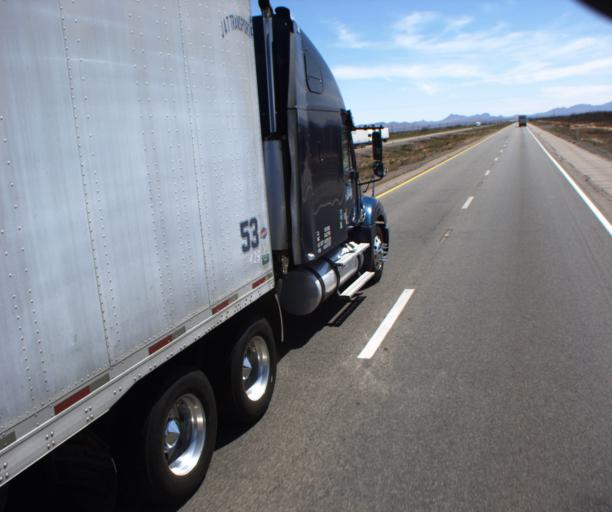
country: US
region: Arizona
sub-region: Cochise County
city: Willcox
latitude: 32.2824
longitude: -109.2894
